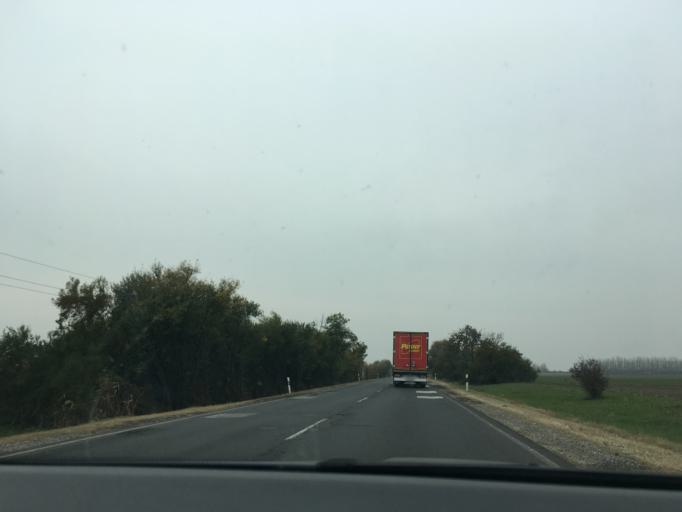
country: HU
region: Jasz-Nagykun-Szolnok
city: Fegyvernek
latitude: 47.2362
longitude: 20.5803
